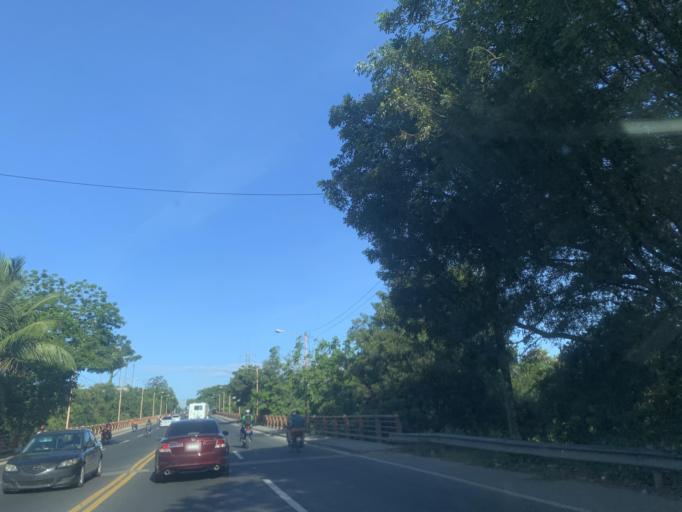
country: DO
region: San Cristobal
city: El Carril
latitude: 18.4320
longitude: -70.0074
